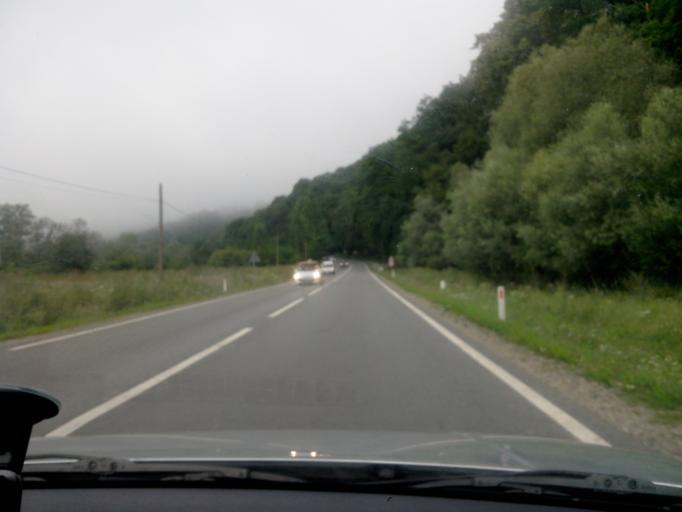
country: RO
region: Salaj
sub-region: Comuna Galgau
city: Galgau
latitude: 47.2833
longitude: 23.6849
